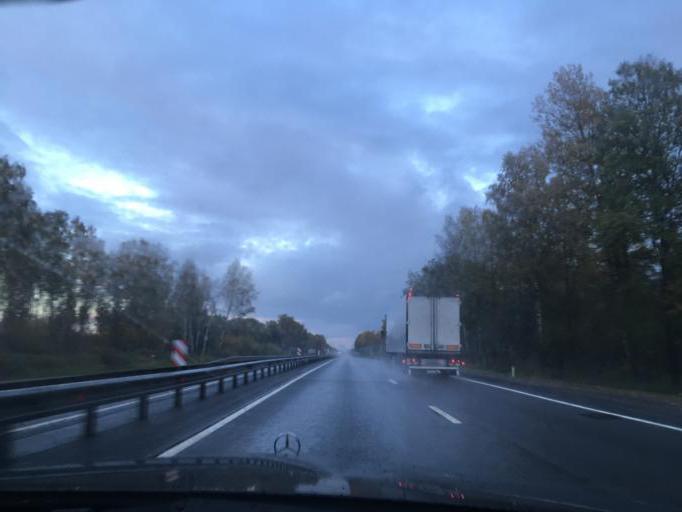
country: RU
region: Smolensk
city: Yartsevo
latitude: 55.0981
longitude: 32.8797
